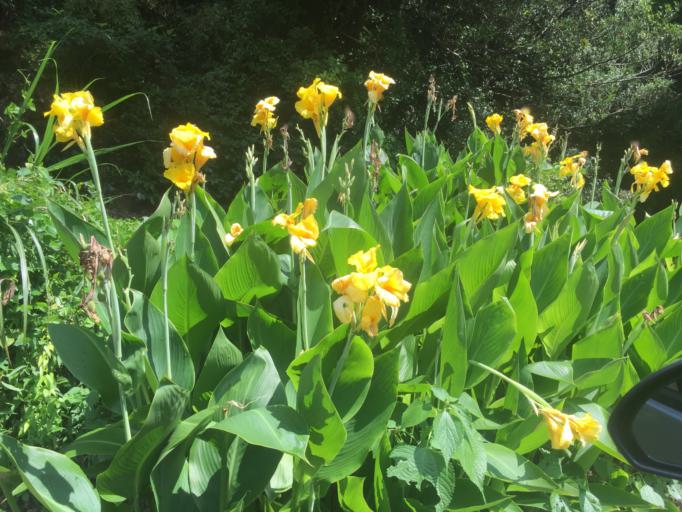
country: JP
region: Shizuoka
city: Kanaya
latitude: 34.8549
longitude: 138.0583
